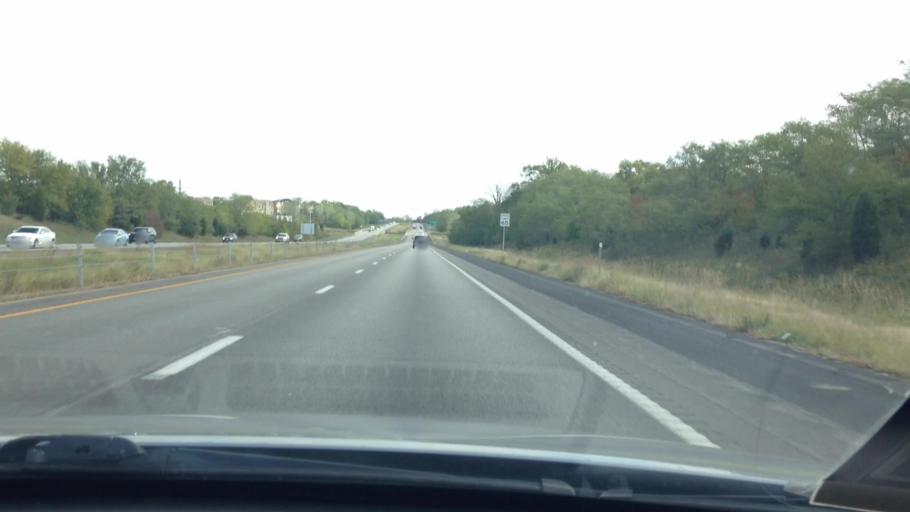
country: US
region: Missouri
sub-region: Platte County
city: Weatherby Lake
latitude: 39.2540
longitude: -94.6233
